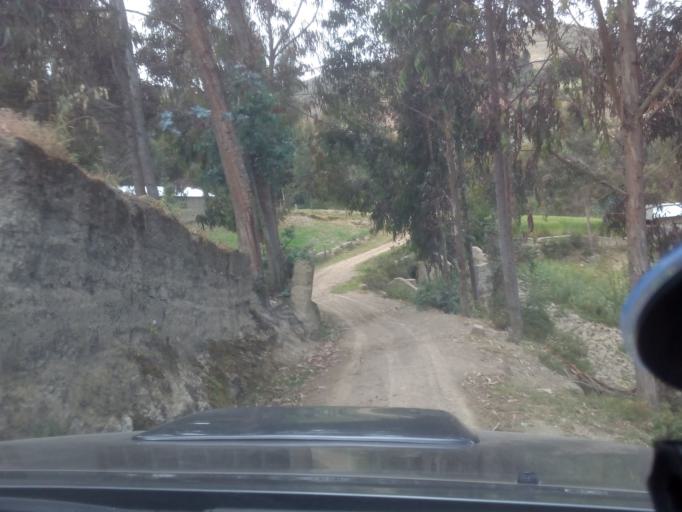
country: PE
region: Ayacucho
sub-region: Provincia de Huanta
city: Luricocha
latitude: -12.8830
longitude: -74.2171
